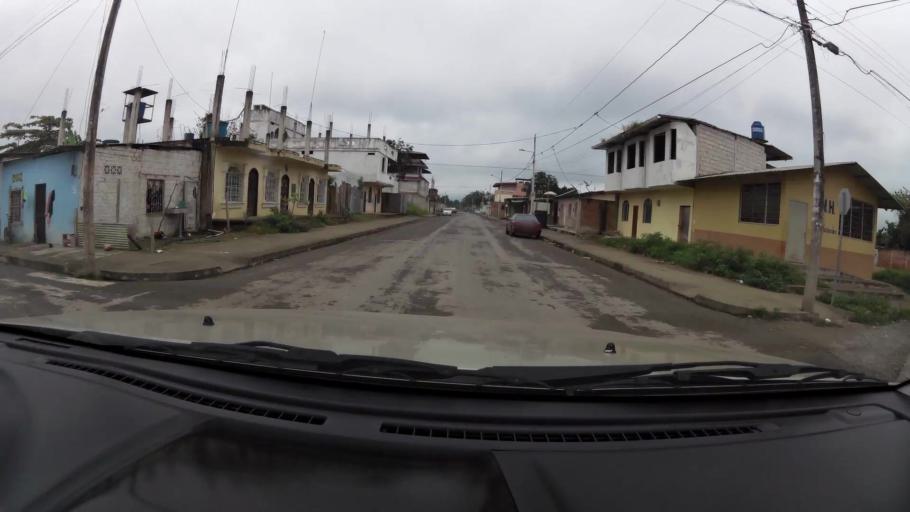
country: EC
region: El Oro
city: Pasaje
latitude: -3.3352
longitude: -79.8077
